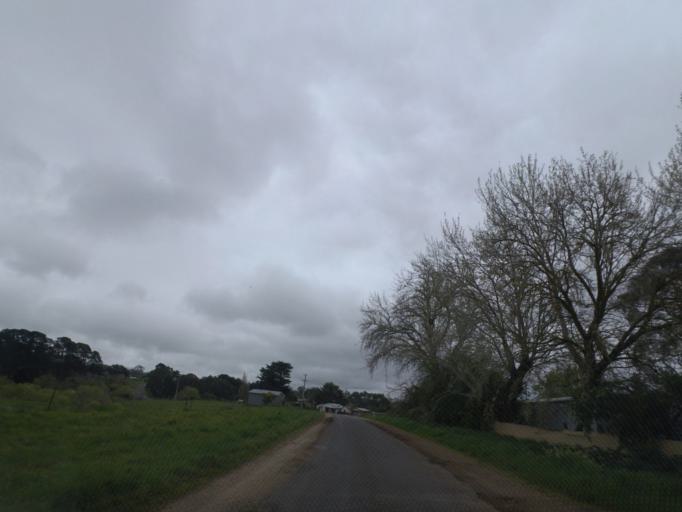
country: AU
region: Victoria
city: Brown Hill
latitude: -37.5908
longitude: 144.0589
